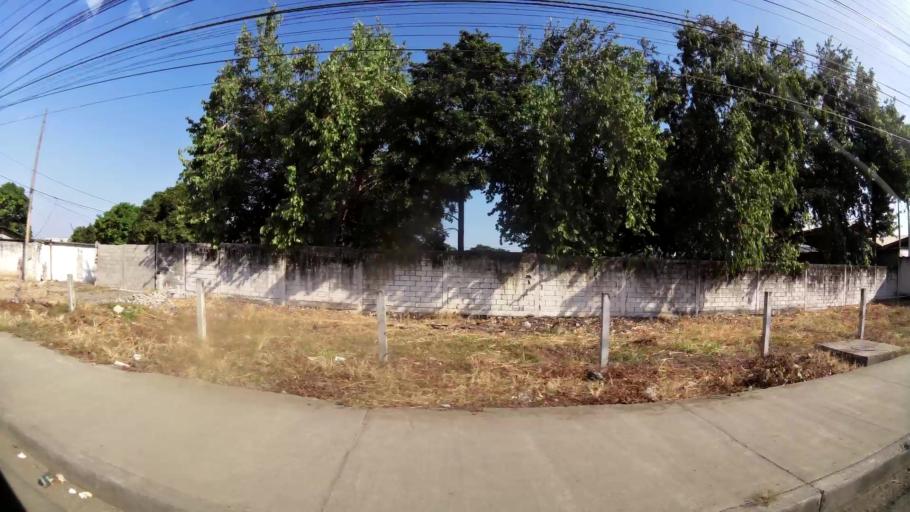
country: EC
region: Guayas
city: Santa Lucia
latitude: -2.1849
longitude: -79.9763
